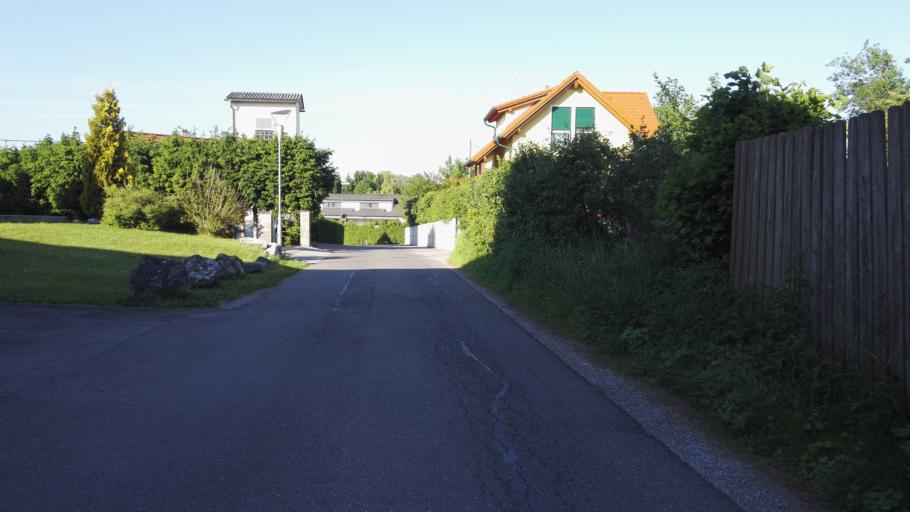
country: AT
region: Styria
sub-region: Politischer Bezirk Graz-Umgebung
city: Feldkirchen bei Graz
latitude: 47.0036
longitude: 15.4496
